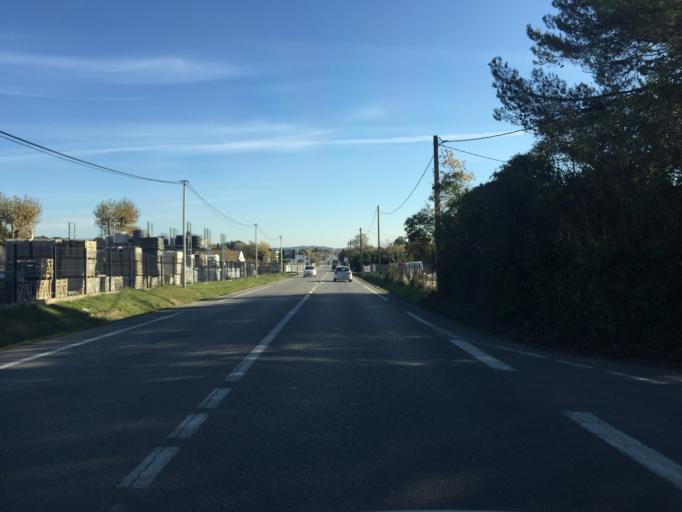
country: FR
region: Provence-Alpes-Cote d'Azur
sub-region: Departement des Bouches-du-Rhone
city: Eguilles
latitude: 43.5843
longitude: 5.3725
